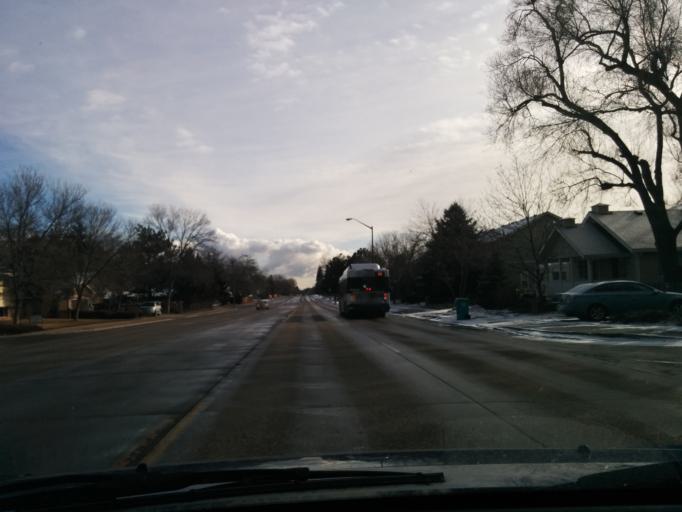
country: US
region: Colorado
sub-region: Larimer County
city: Fort Collins
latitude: 40.5674
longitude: -105.1099
